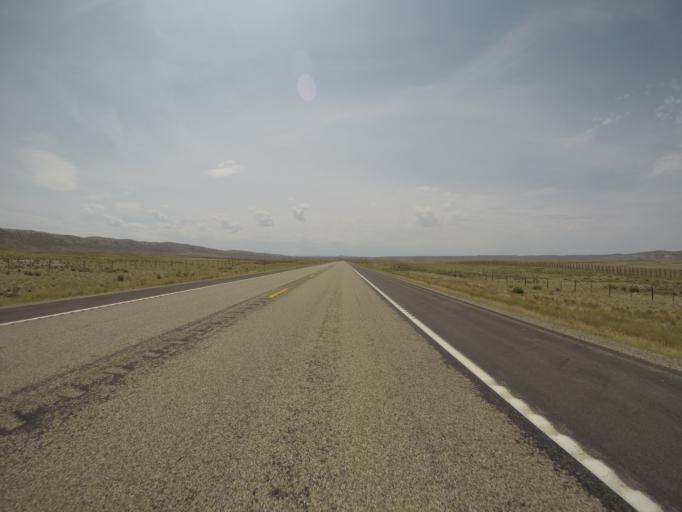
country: US
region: Wyoming
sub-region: Lincoln County
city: Kemmerer
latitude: 41.6541
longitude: -110.5707
